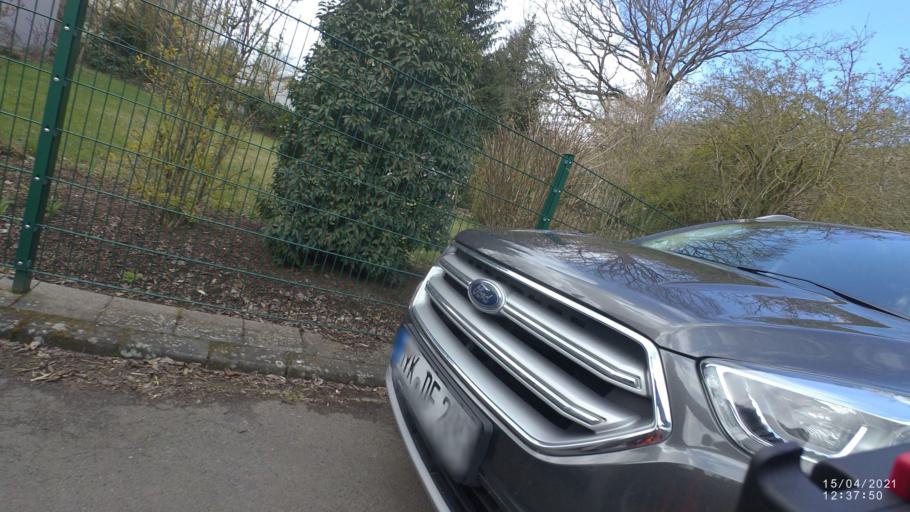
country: DE
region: Rheinland-Pfalz
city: Mendig
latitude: 50.3594
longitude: 7.2724
